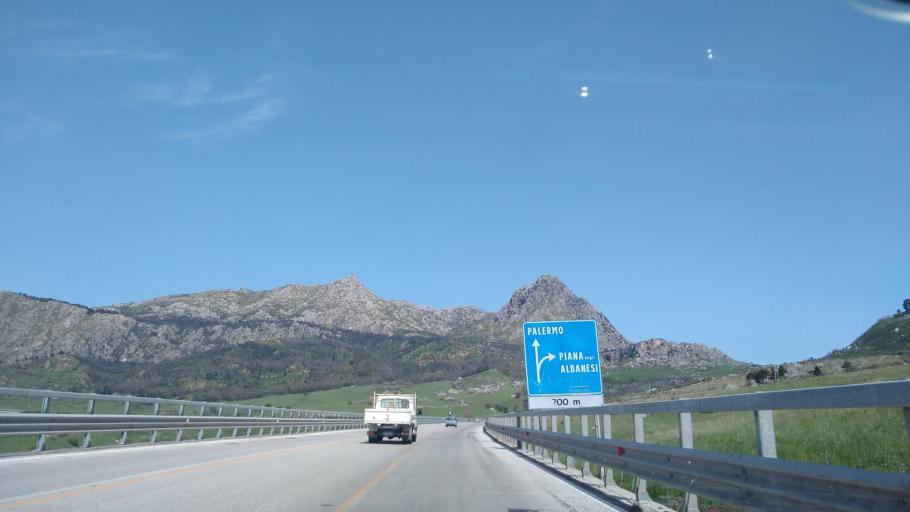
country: IT
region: Sicily
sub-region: Palermo
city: San Giuseppe Jato
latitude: 37.9809
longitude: 13.2279
